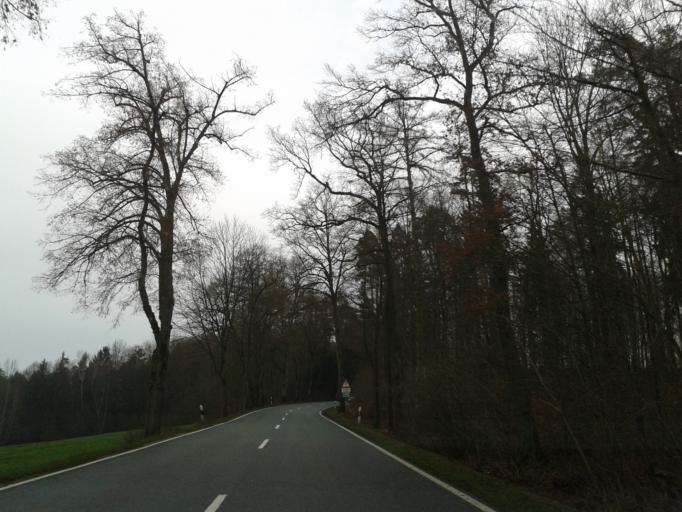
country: DE
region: Bavaria
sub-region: Upper Franconia
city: Weitramsdorf
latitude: 50.2327
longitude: 10.8788
